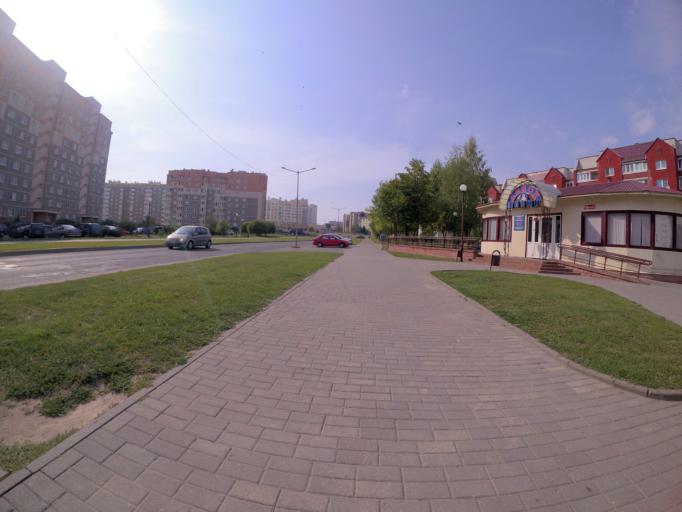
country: BY
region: Grodnenskaya
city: Hrodna
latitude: 53.7106
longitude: 23.8563
